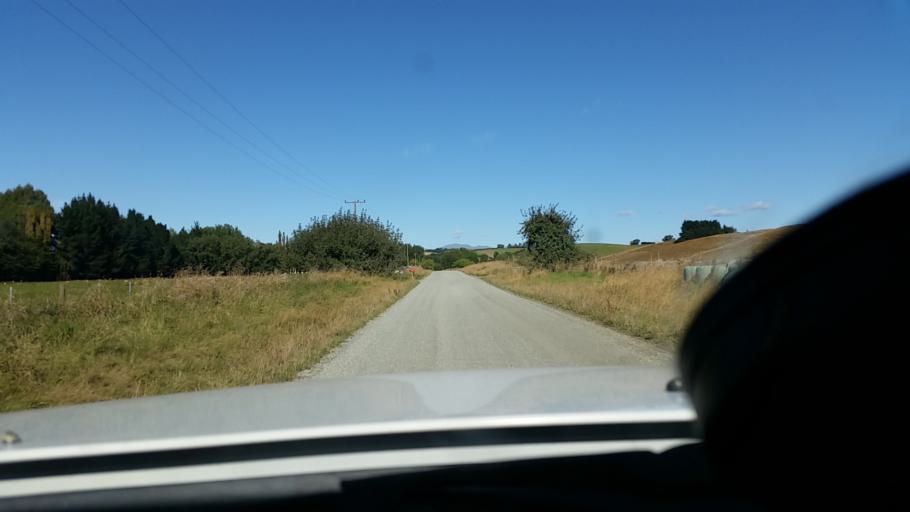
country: NZ
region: Canterbury
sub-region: Timaru District
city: Pleasant Point
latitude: -44.3387
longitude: 171.1760
